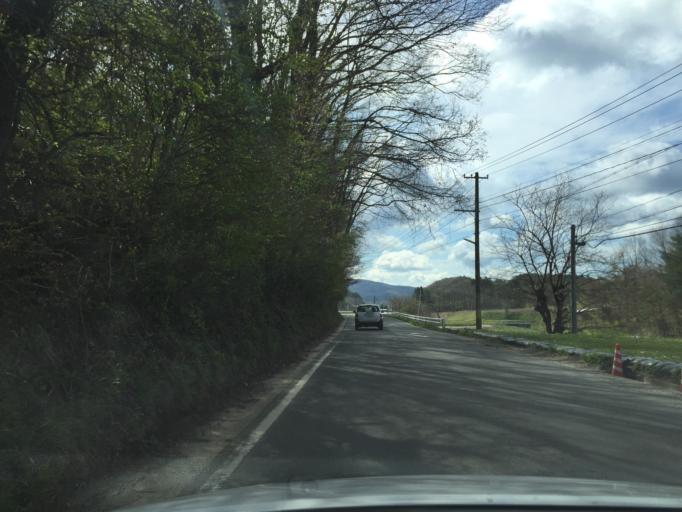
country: JP
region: Fukushima
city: Funehikimachi-funehiki
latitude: 37.6082
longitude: 140.6657
